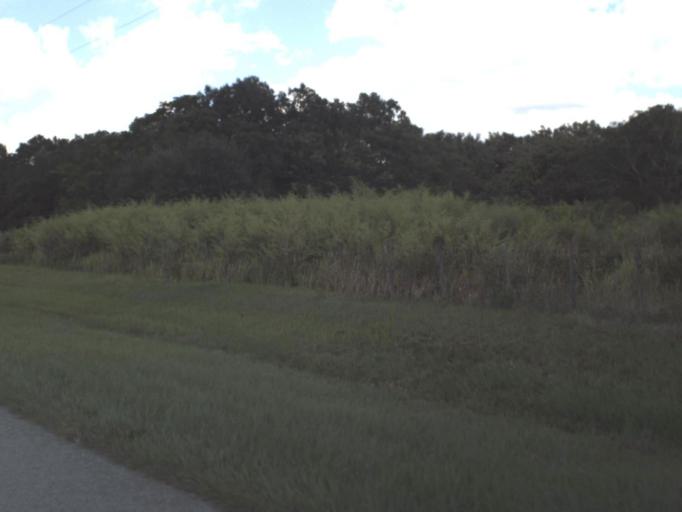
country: US
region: Florida
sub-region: Highlands County
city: Sebring
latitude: 27.4244
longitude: -81.5780
